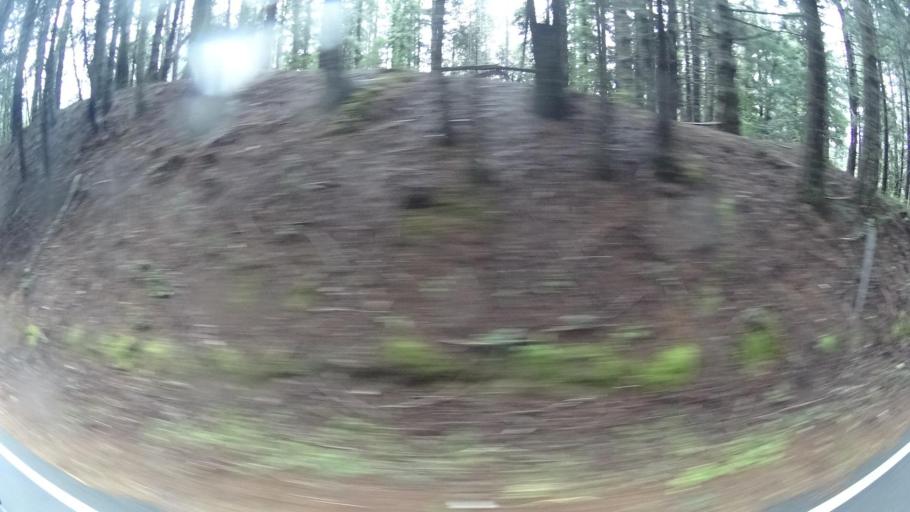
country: US
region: California
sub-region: Humboldt County
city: Westhaven-Moonstone
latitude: 41.2090
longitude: -123.9555
